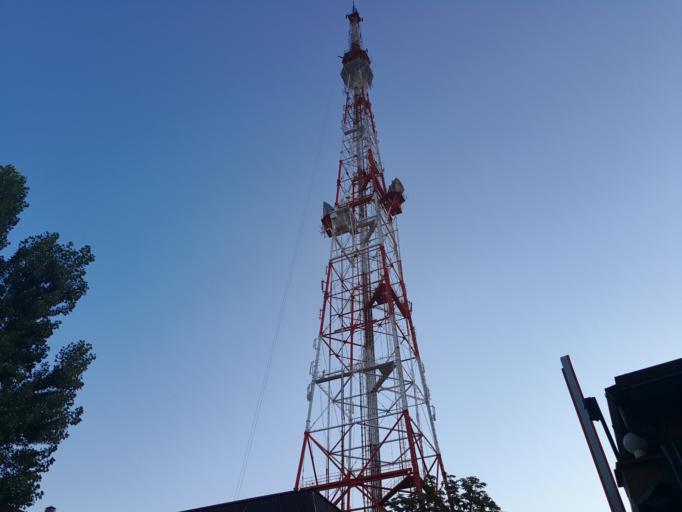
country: RU
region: Krasnodarskiy
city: Krasnodar
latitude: 45.0274
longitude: 39.0010
